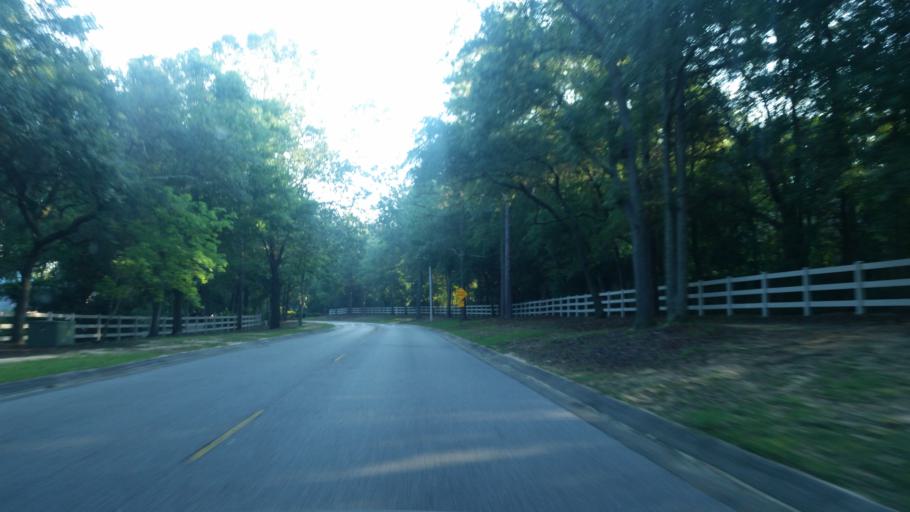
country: US
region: Florida
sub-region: Escambia County
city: Ensley
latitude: 30.5406
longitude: -87.2395
